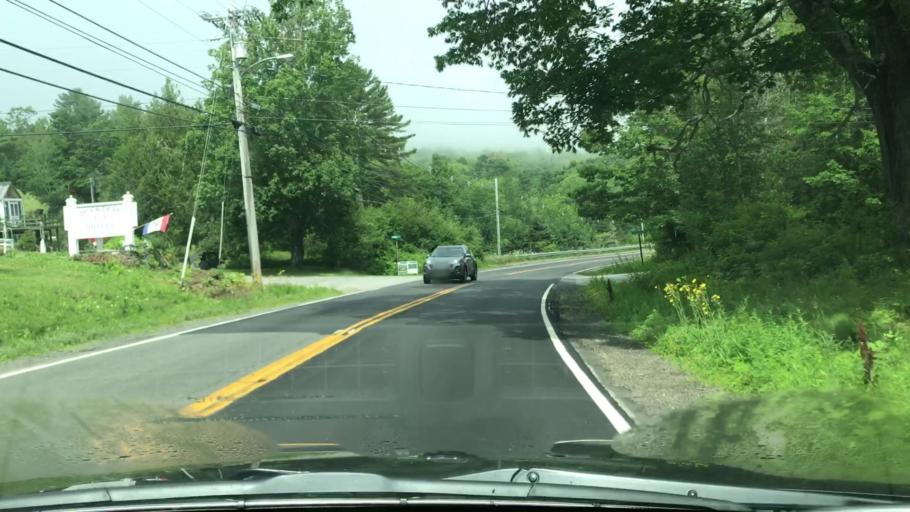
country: US
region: Maine
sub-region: Waldo County
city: Lincolnville
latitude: 44.2966
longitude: -69.0066
